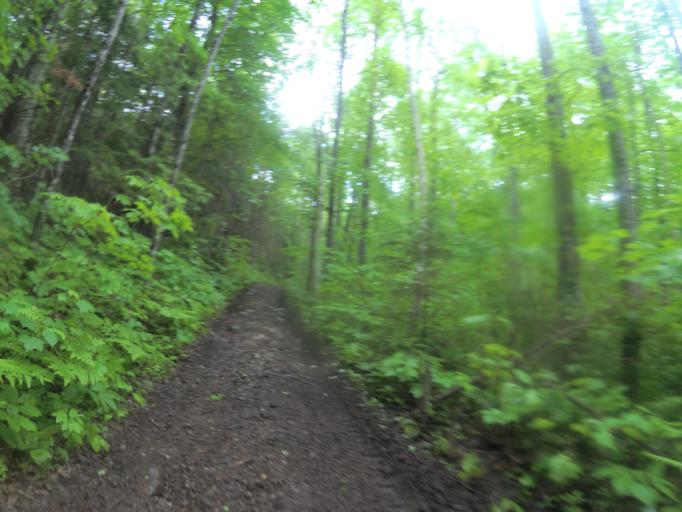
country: CA
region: Ontario
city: Renfrew
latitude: 45.1358
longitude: -76.8192
